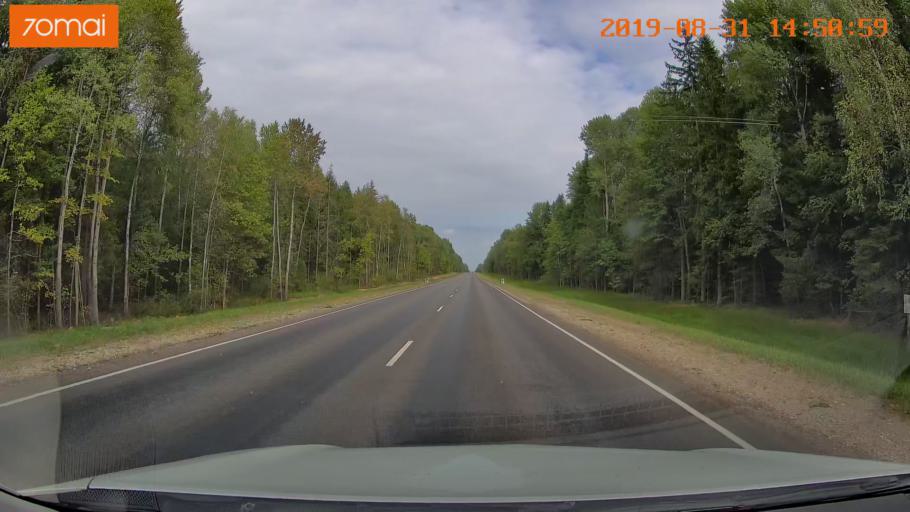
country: RU
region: Kaluga
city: Spas-Demensk
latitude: 54.2653
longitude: 33.8033
